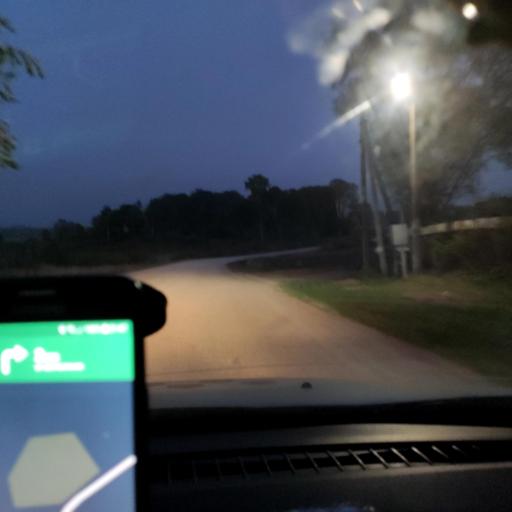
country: RU
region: Bashkortostan
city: Kabakovo
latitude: 54.6676
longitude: 56.2806
